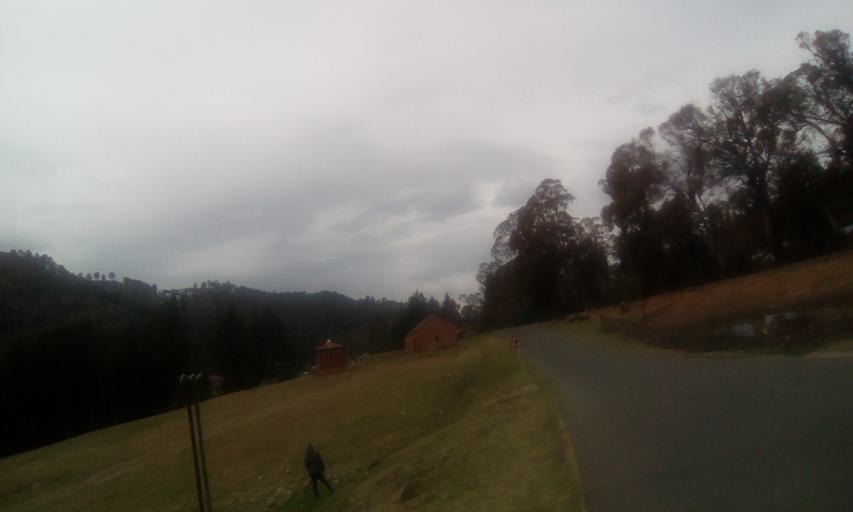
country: LS
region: Qacha's Nek
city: Qacha's Nek
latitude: -30.1202
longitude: 28.6894
